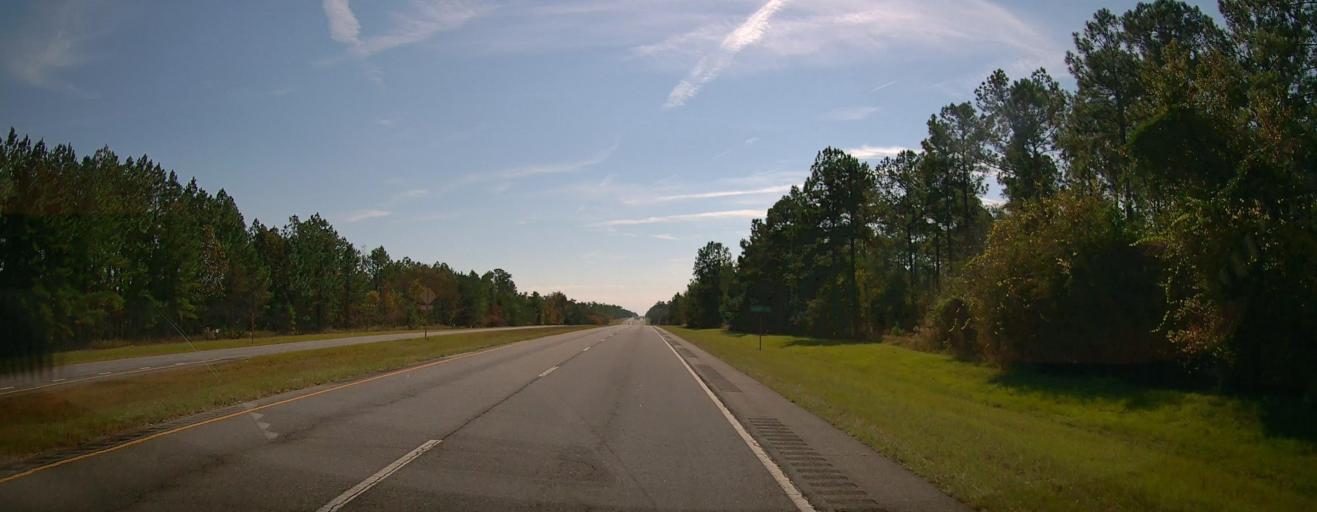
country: US
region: Georgia
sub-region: Lee County
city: Leesburg
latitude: 31.7246
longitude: -83.9876
